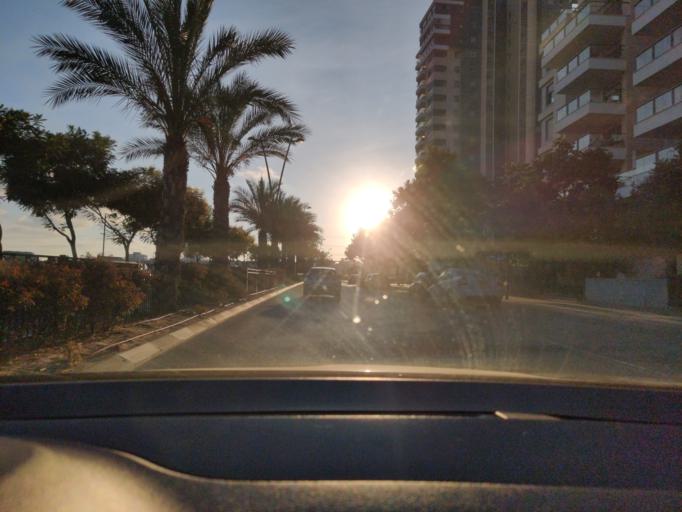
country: IL
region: Central District
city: Elyakhin
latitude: 32.4270
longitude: 34.9372
